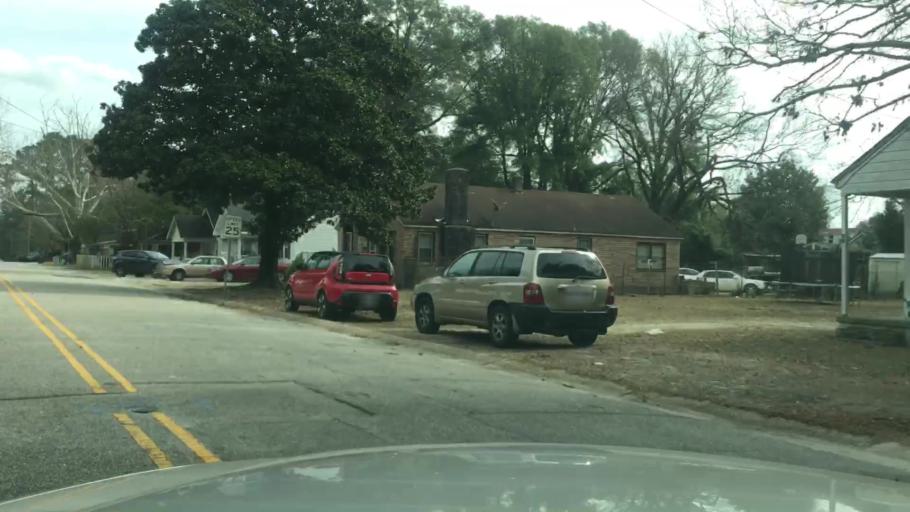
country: US
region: North Carolina
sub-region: Cumberland County
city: Fayetteville
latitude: 35.0527
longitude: -78.8993
